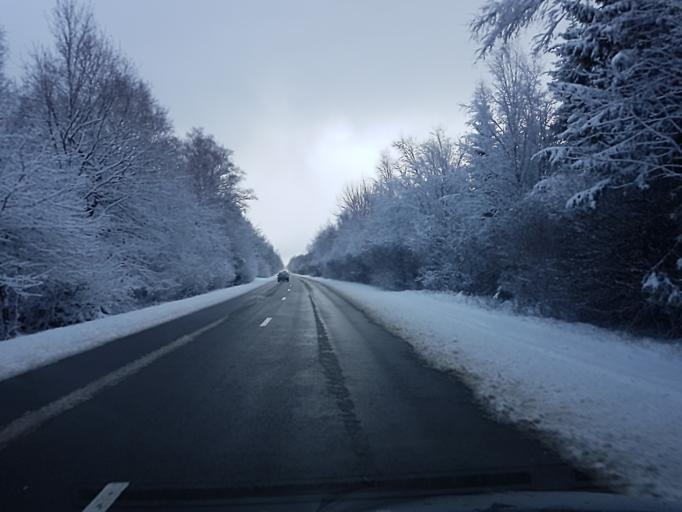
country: BE
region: Wallonia
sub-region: Province de Liege
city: Jalhay
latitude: 50.5442
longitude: 6.0114
